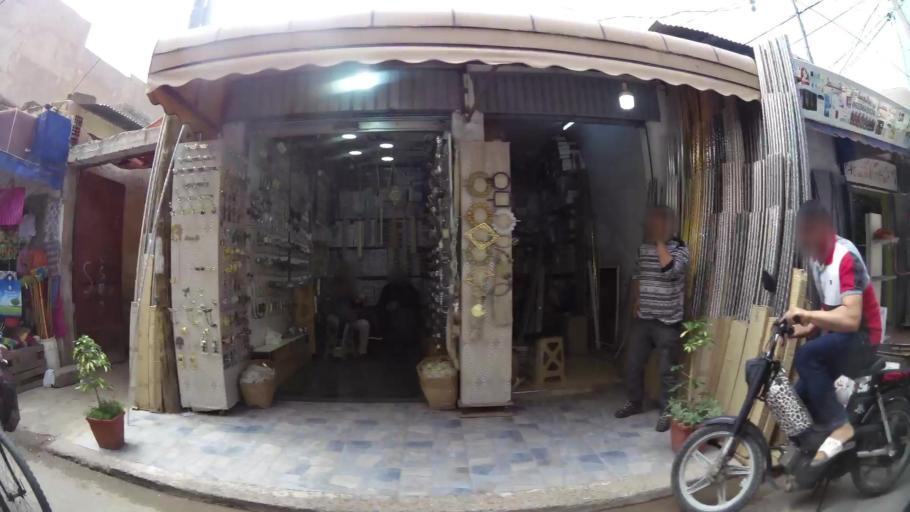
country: MA
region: Oriental
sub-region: Oujda-Angad
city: Oujda
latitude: 34.6813
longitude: -1.9045
